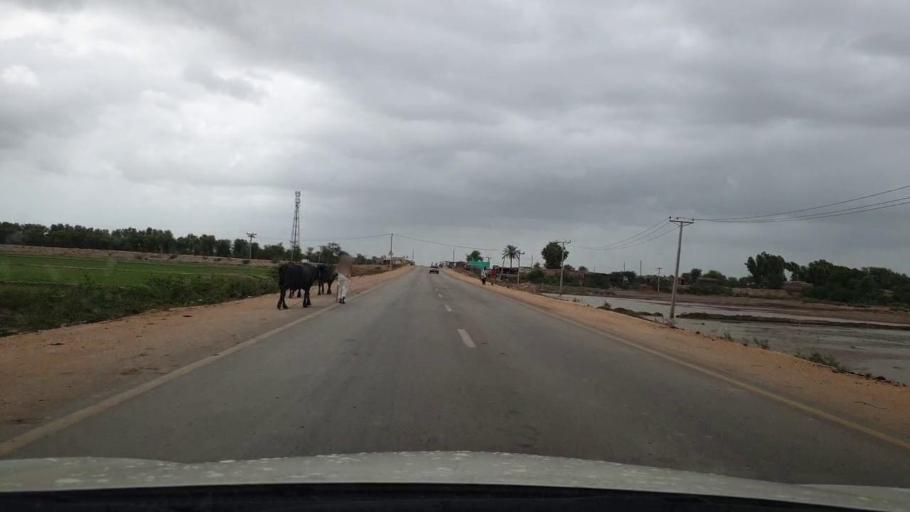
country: PK
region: Sindh
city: Badin
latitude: 24.6555
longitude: 68.7269
